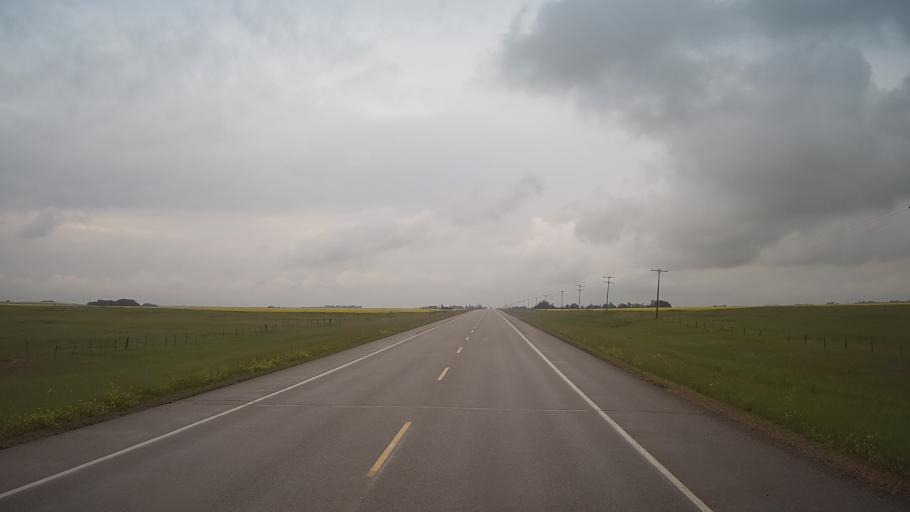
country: CA
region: Saskatchewan
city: Unity
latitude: 52.4349
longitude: -109.0019
